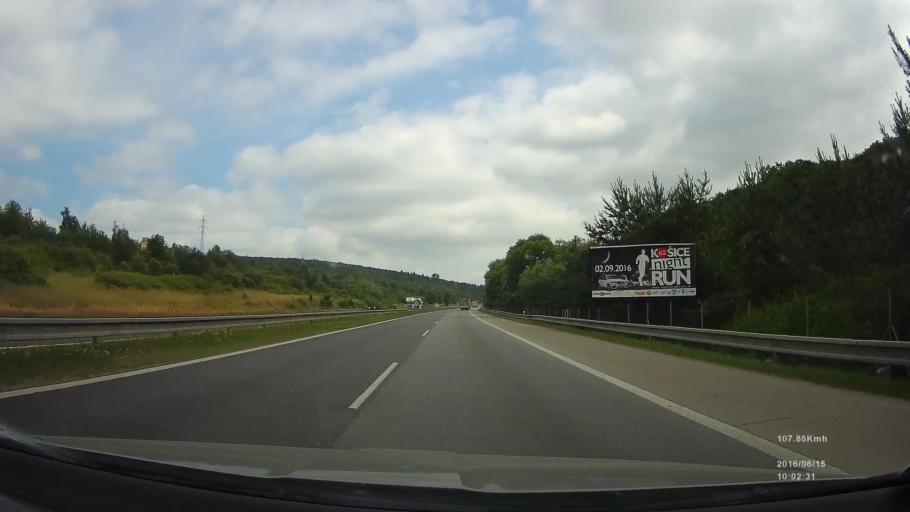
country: SK
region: Kosicky
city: Kosice
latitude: 48.7514
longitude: 21.2771
